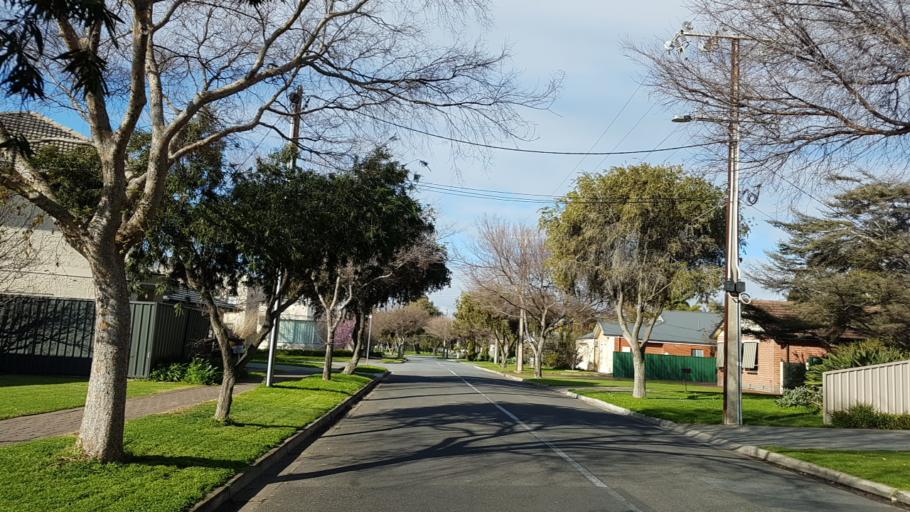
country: AU
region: South Australia
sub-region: Charles Sturt
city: Henley Beach
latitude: -34.9327
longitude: 138.5053
